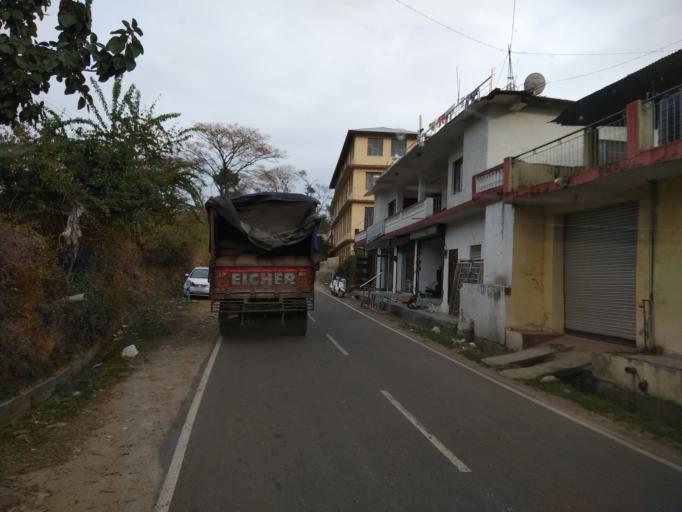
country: IN
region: Himachal Pradesh
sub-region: Kangra
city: Palampur
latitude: 32.1147
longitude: 76.5154
